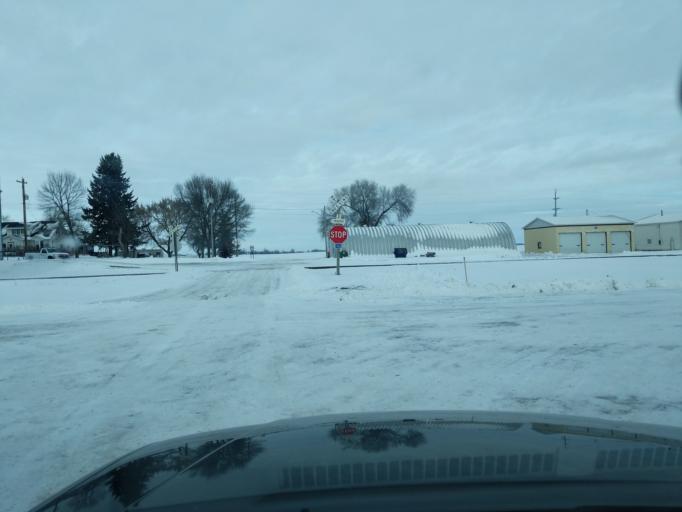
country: US
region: Minnesota
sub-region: Renville County
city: Renville
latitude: 44.7878
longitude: -95.3500
